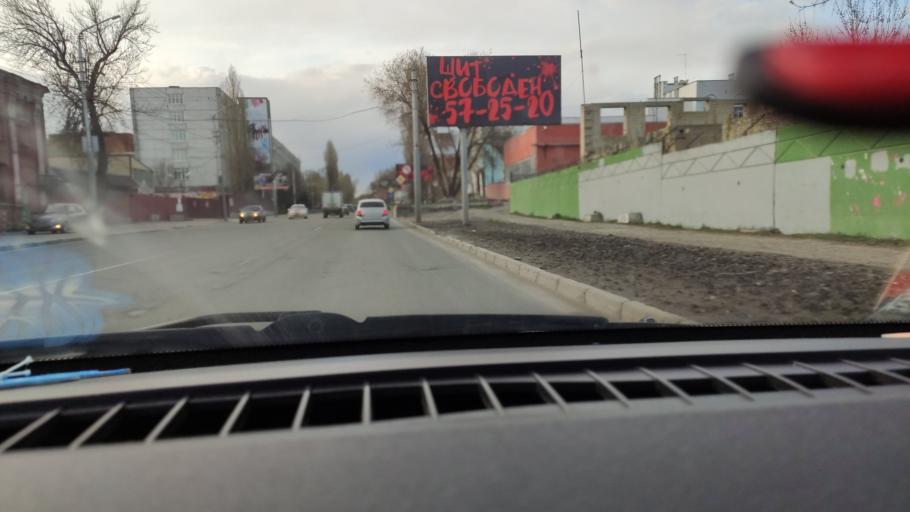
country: RU
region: Saratov
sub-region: Saratovskiy Rayon
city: Saratov
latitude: 51.5517
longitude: 46.0102
